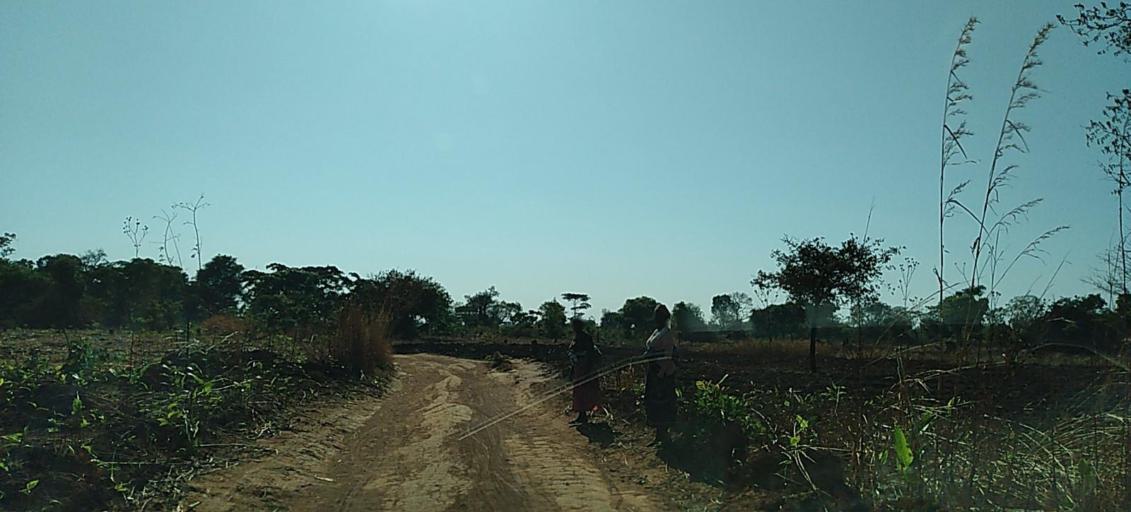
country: ZM
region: Copperbelt
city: Chililabombwe
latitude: -12.3705
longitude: 27.9041
